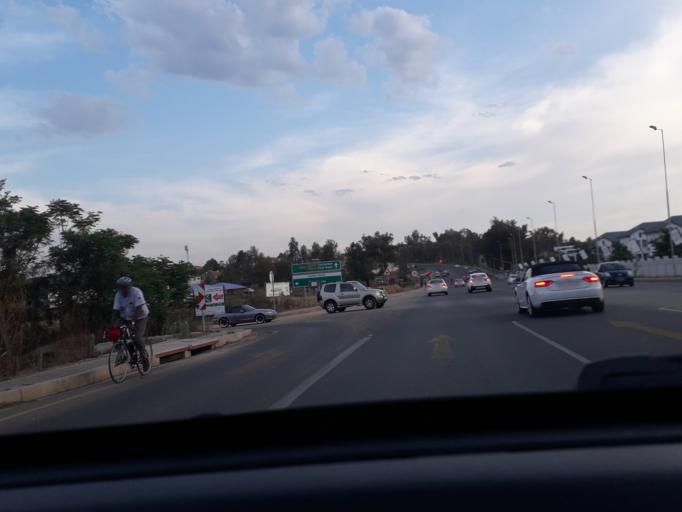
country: ZA
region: Gauteng
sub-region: City of Johannesburg Metropolitan Municipality
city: Diepsloot
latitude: -25.9927
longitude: 27.9835
